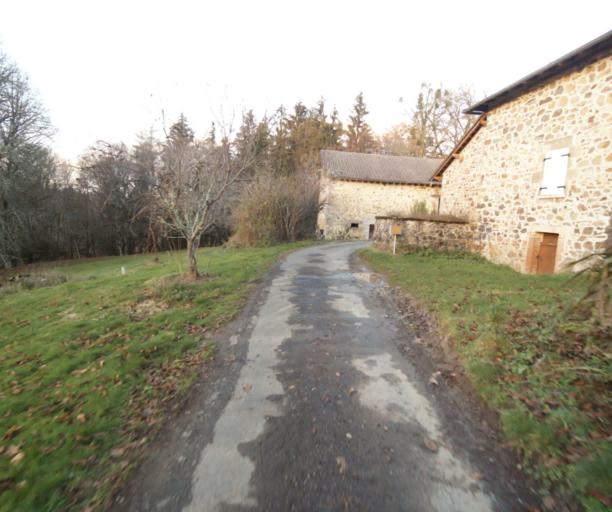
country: FR
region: Limousin
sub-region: Departement de la Correze
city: Laguenne
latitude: 45.2334
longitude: 1.7765
